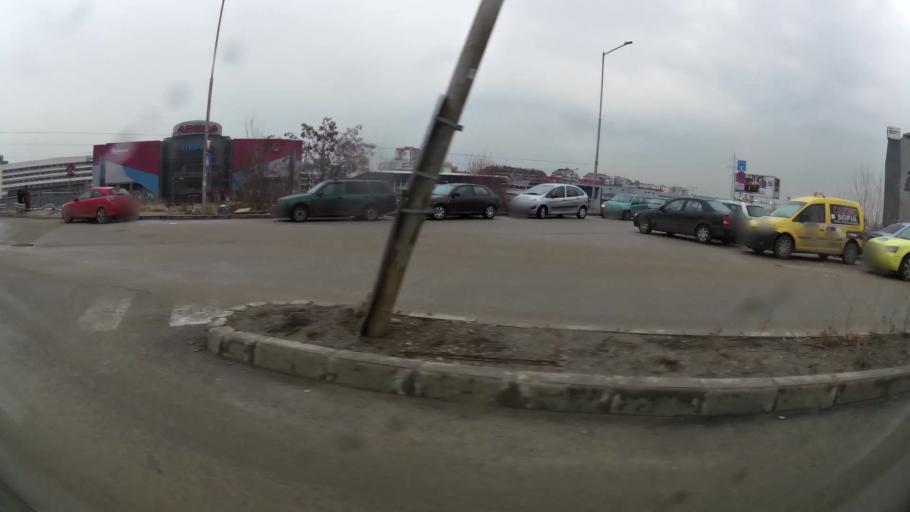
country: BG
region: Sofia-Capital
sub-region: Stolichna Obshtina
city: Sofia
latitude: 42.6229
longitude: 23.3763
